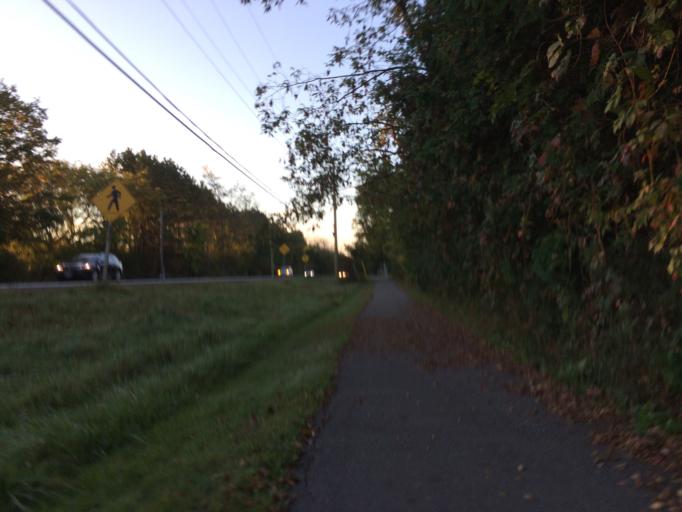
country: CA
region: Ontario
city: Ottawa
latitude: 45.2699
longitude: -75.5752
